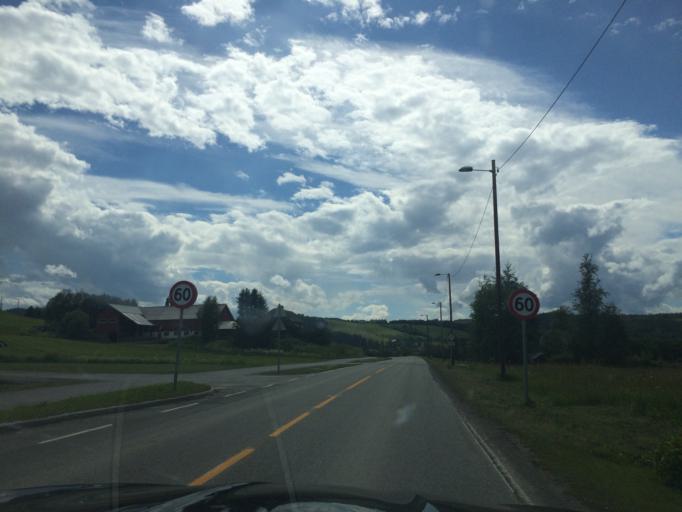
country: NO
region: Sor-Trondelag
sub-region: Selbu
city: Mebonden
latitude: 63.2492
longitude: 11.0938
